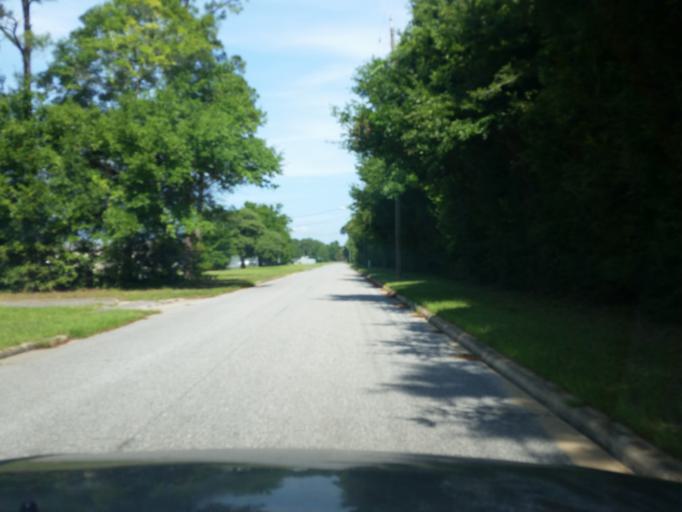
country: US
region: Florida
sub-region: Escambia County
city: Ferry Pass
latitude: 30.5315
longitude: -87.1957
